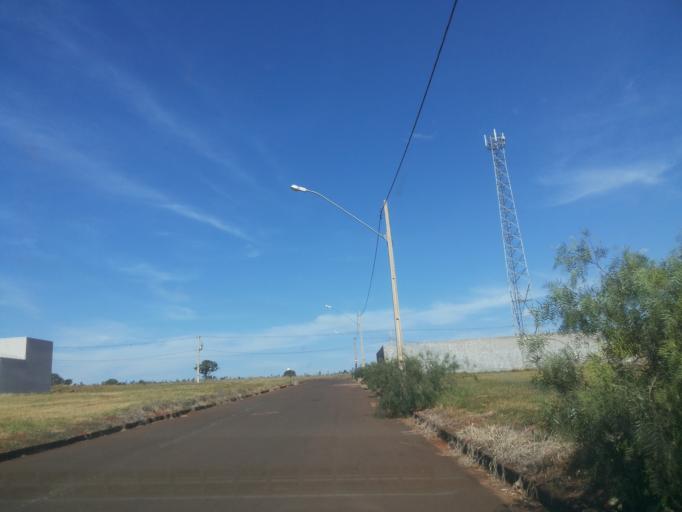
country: BR
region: Minas Gerais
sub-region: Ituiutaba
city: Ituiutaba
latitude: -19.0025
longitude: -49.4616
